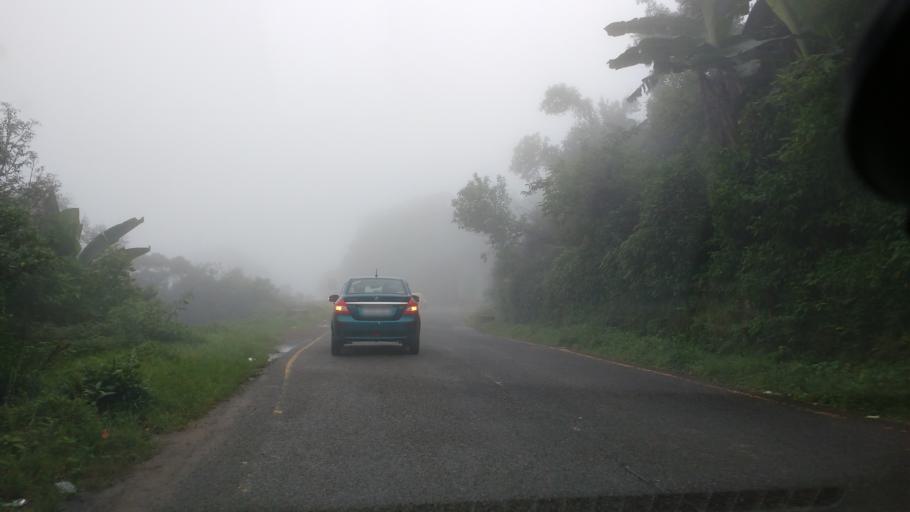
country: IN
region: Meghalaya
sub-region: East Khasi Hills
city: Cherrapunji
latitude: 25.2864
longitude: 91.7185
